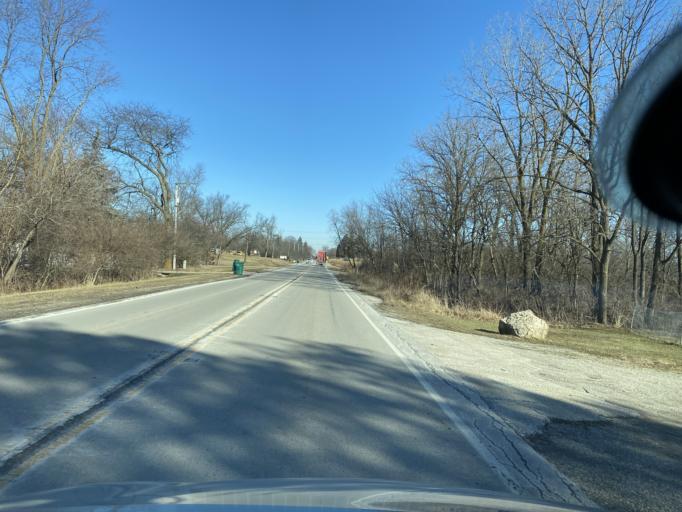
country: US
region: Illinois
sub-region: Will County
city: Goodings Grove
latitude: 41.6791
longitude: -87.9421
